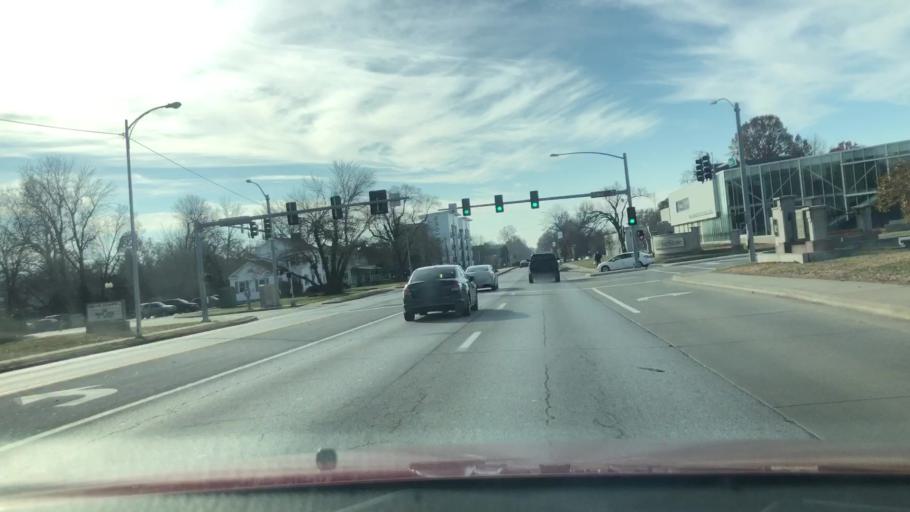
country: US
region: Missouri
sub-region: Greene County
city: Springfield
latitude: 37.2018
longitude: -93.2762
